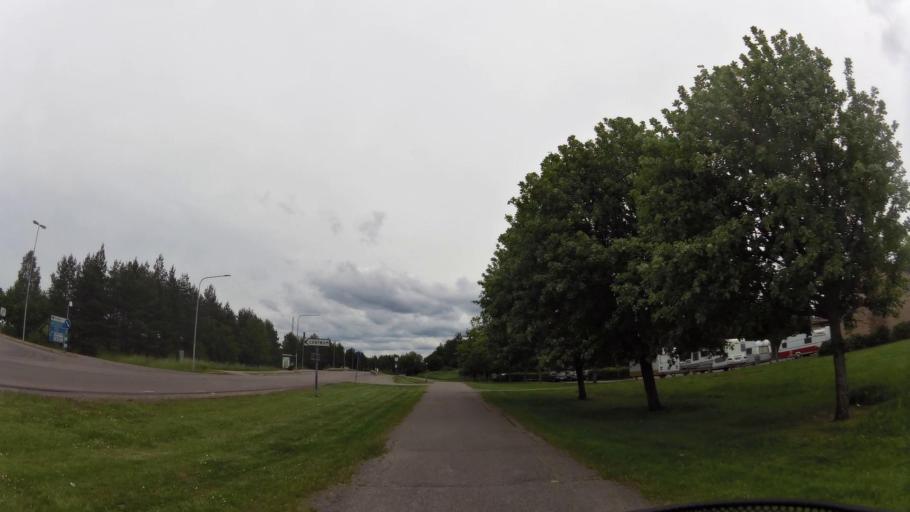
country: SE
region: OEstergoetland
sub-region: Linkopings Kommun
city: Malmslatt
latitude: 58.3897
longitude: 15.5654
